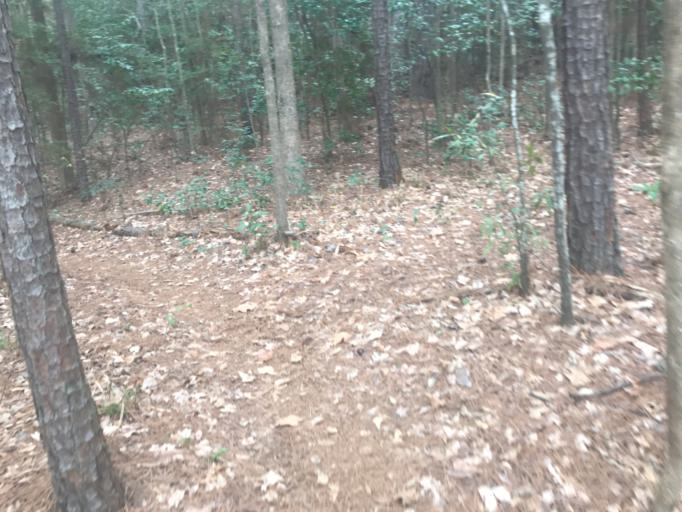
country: US
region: Texas
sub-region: Nacogdoches County
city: Nacogdoches
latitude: 31.6220
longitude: -94.6381
